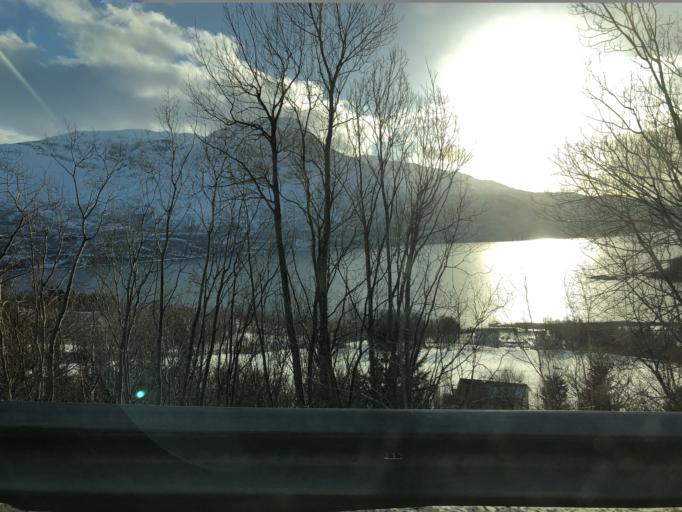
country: NO
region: Nordland
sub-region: Narvik
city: Bjerkvik
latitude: 68.4737
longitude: 17.6514
